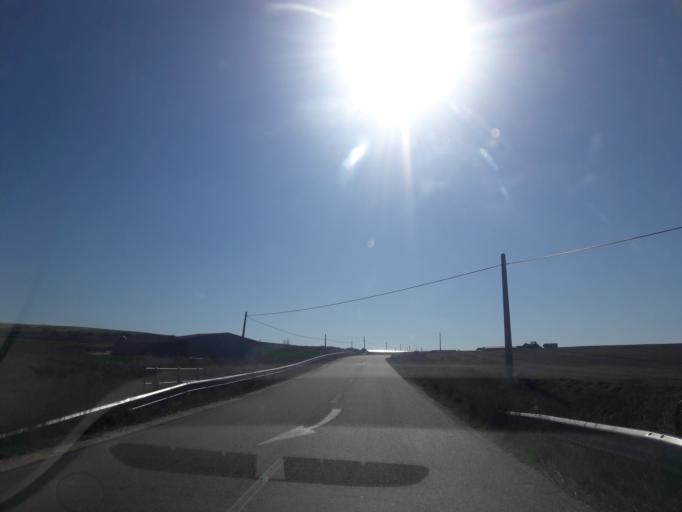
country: ES
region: Castille and Leon
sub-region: Provincia de Salamanca
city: Tordillos
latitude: 40.8534
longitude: -5.3444
